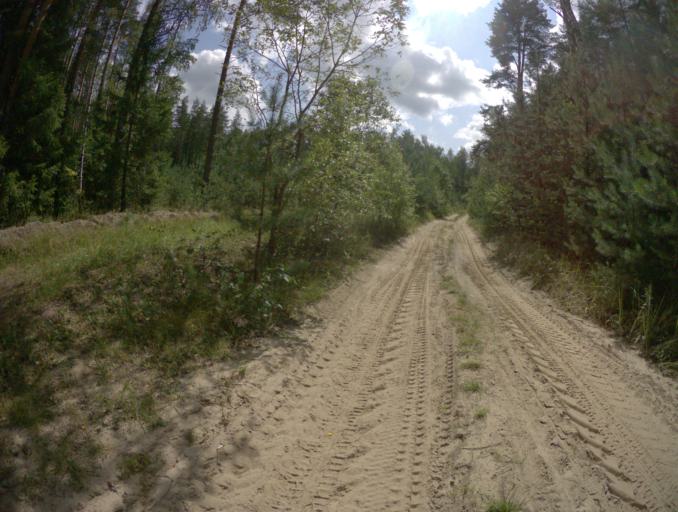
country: RU
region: Vladimir
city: Vorsha
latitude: 55.9628
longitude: 40.1573
